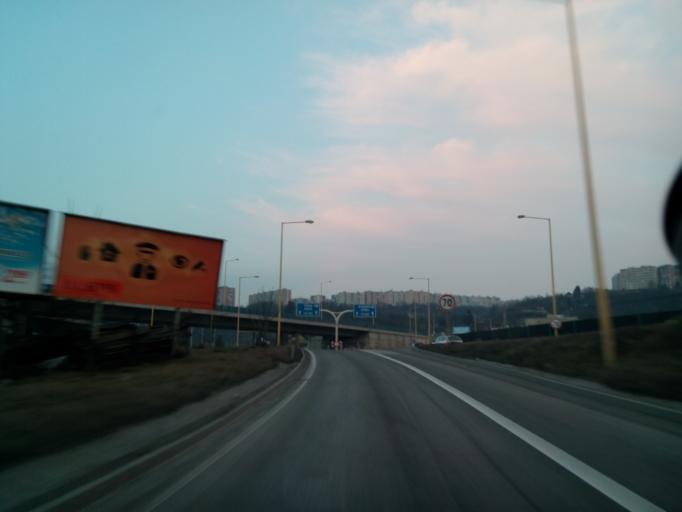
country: SK
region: Kosicky
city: Kosice
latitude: 48.7239
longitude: 21.2759
